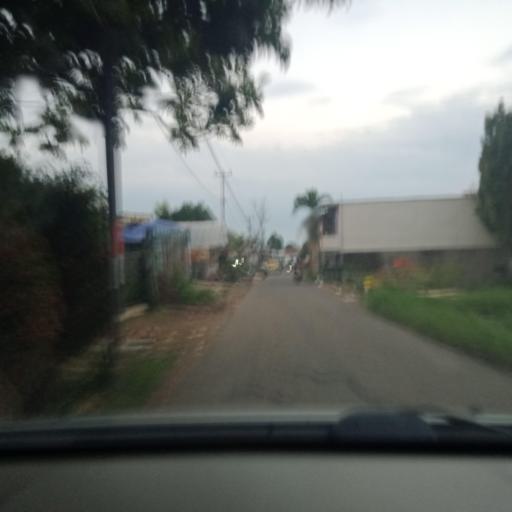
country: ID
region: West Java
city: Lembang
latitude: -6.8280
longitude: 107.5844
